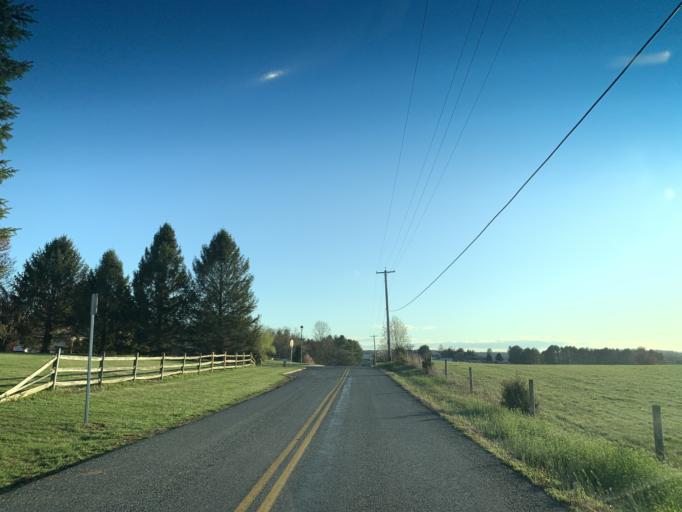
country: US
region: Maryland
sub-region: Harford County
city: South Bel Air
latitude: 39.5943
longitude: -76.2787
